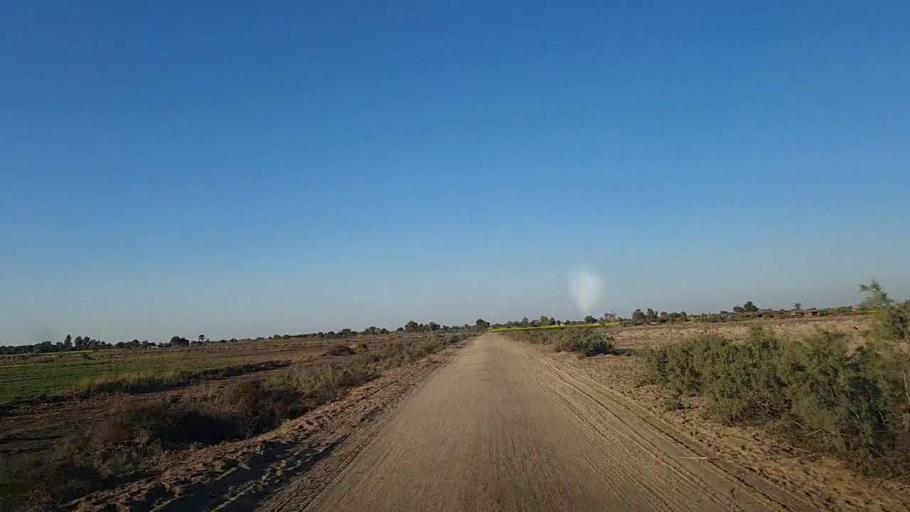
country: PK
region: Sindh
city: Sanghar
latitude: 26.1451
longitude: 68.9265
